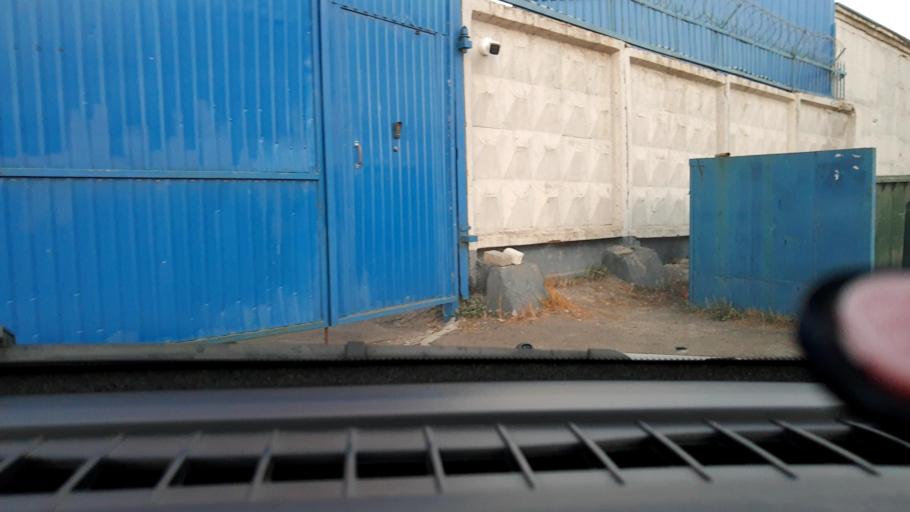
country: RU
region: Nizjnij Novgorod
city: Nizhniy Novgorod
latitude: 56.3039
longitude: 43.9303
